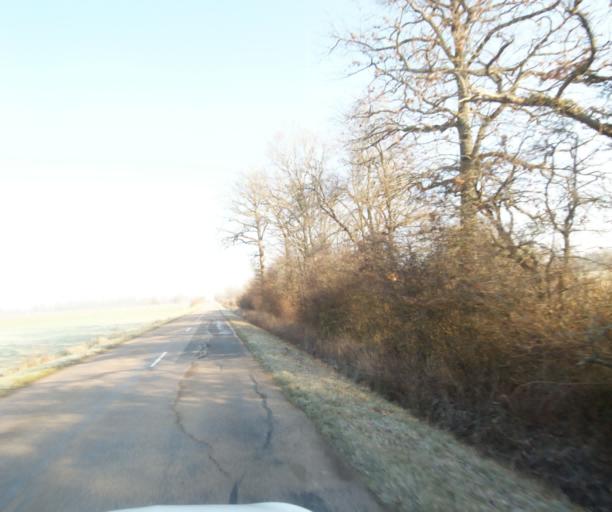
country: FR
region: Champagne-Ardenne
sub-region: Departement de la Haute-Marne
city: Montier-en-Der
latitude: 48.4229
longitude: 4.7467
